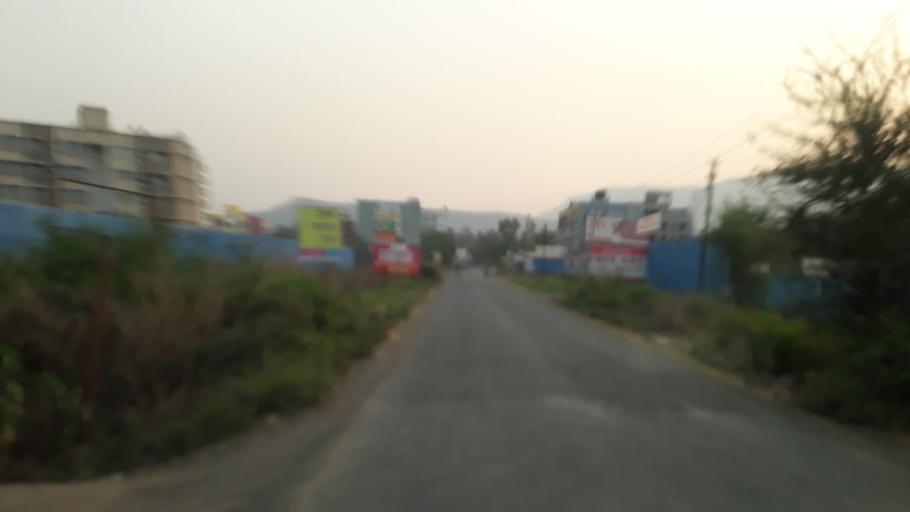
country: IN
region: Maharashtra
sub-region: Raigarh
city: Neral
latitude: 19.0321
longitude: 73.3255
